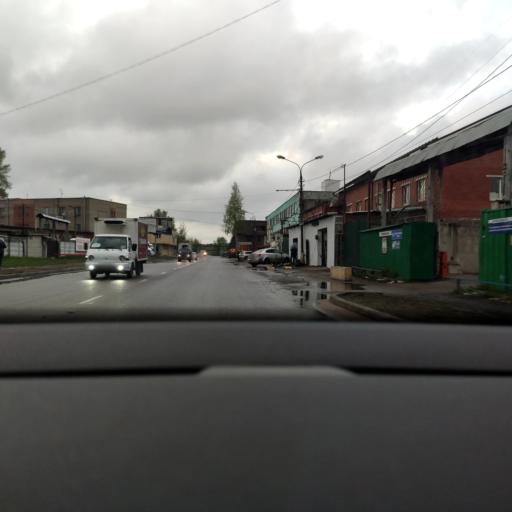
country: RU
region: Moskovskaya
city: Reutov
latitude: 55.7672
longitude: 37.8810
